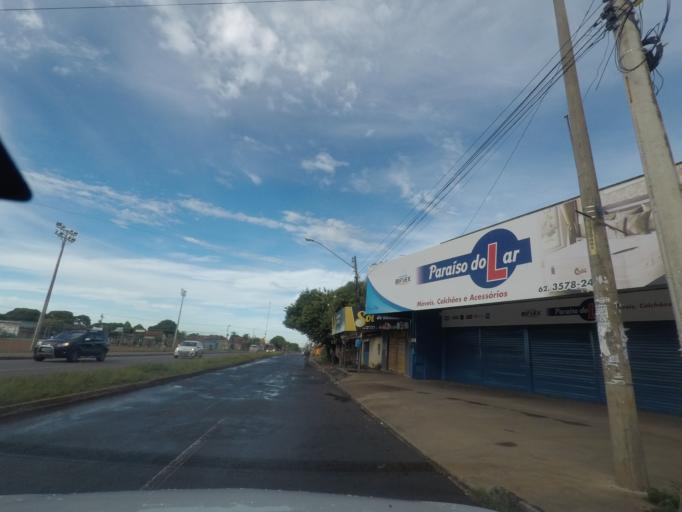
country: BR
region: Goias
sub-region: Aparecida De Goiania
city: Aparecida de Goiania
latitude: -16.7842
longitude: -49.3612
